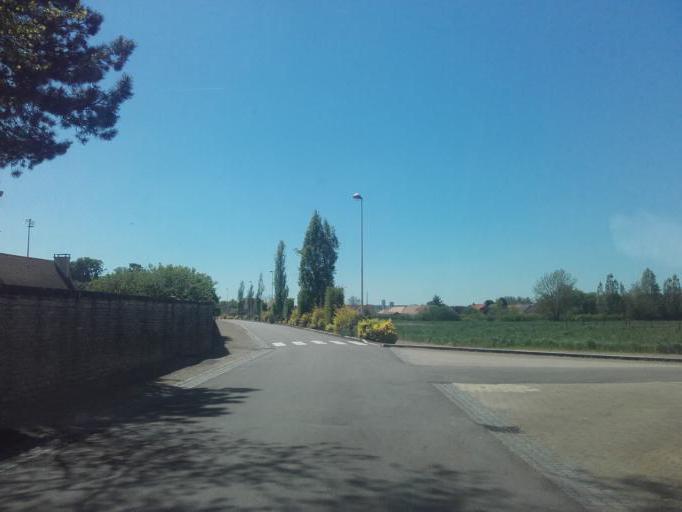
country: FR
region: Bourgogne
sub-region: Departement de la Cote-d'Or
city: Beaune
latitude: 47.0278
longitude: 4.8872
